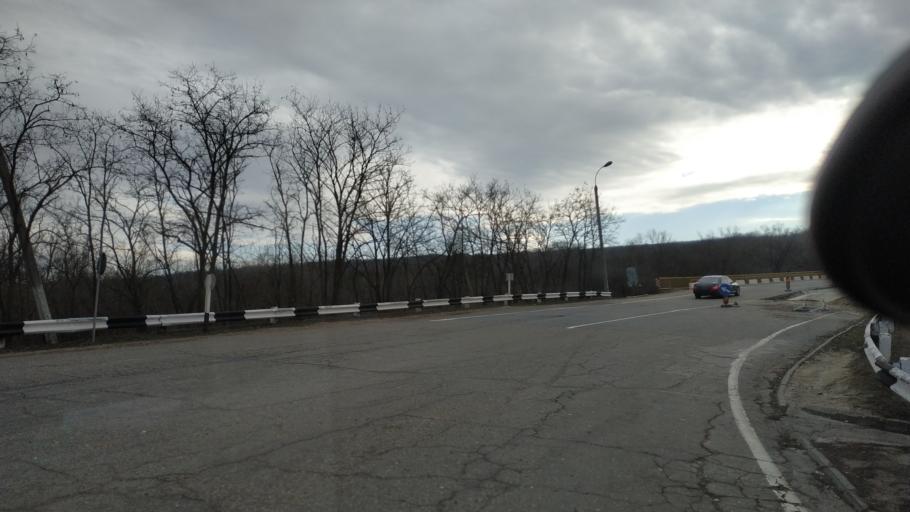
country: MD
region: Chisinau
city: Vadul lui Voda
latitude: 47.0851
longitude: 29.0887
